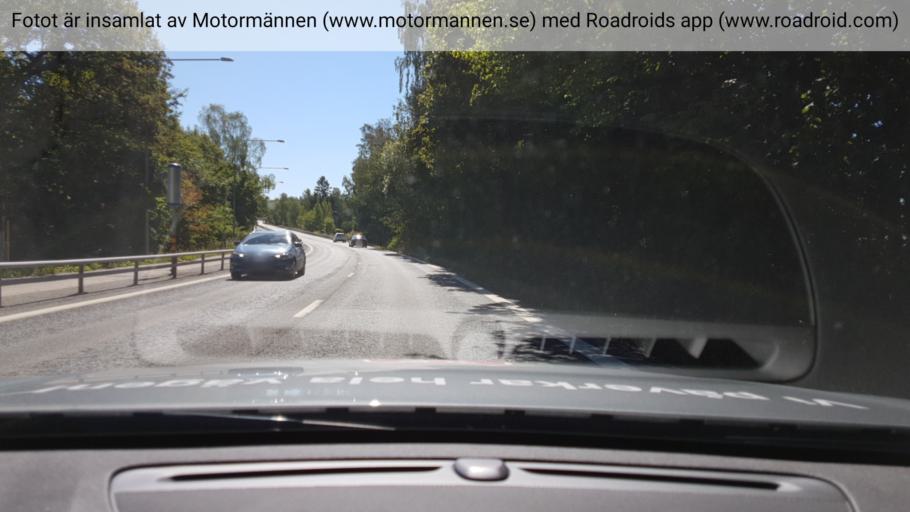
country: SE
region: Stockholm
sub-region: Tyreso Kommun
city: Bollmora
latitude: 59.2185
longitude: 18.2037
